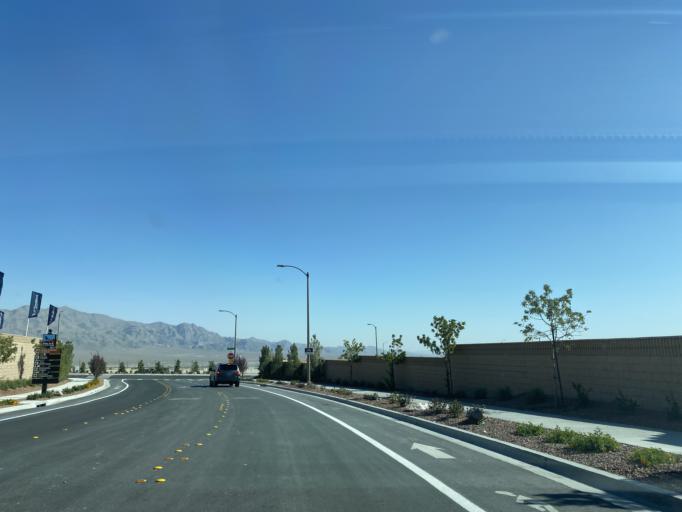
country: US
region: Nevada
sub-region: Clark County
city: Summerlin South
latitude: 36.3167
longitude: -115.3132
